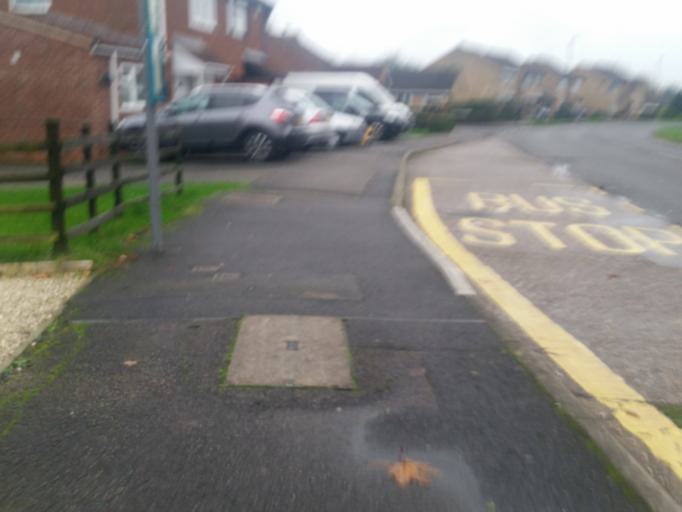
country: GB
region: England
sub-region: Derbyshire
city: Borrowash
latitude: 52.8900
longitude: -1.4107
